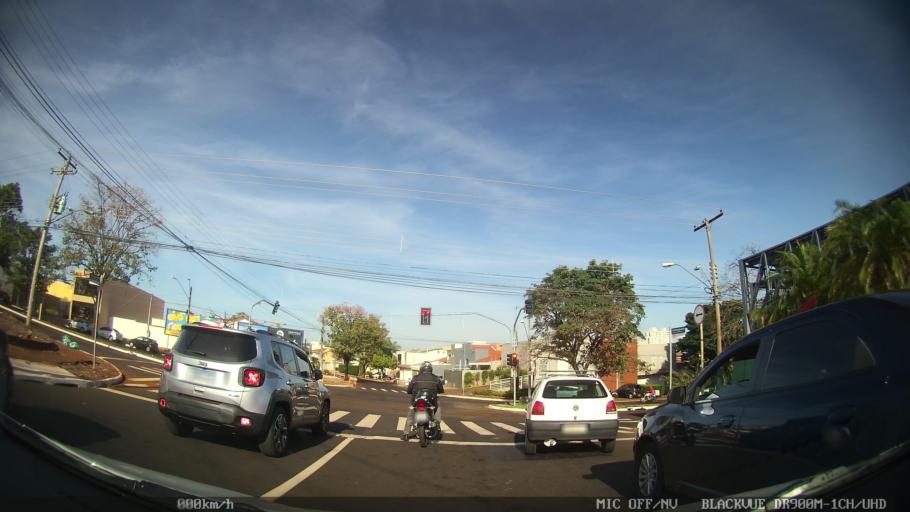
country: BR
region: Sao Paulo
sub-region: Ribeirao Preto
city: Ribeirao Preto
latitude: -21.1978
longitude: -47.8178
